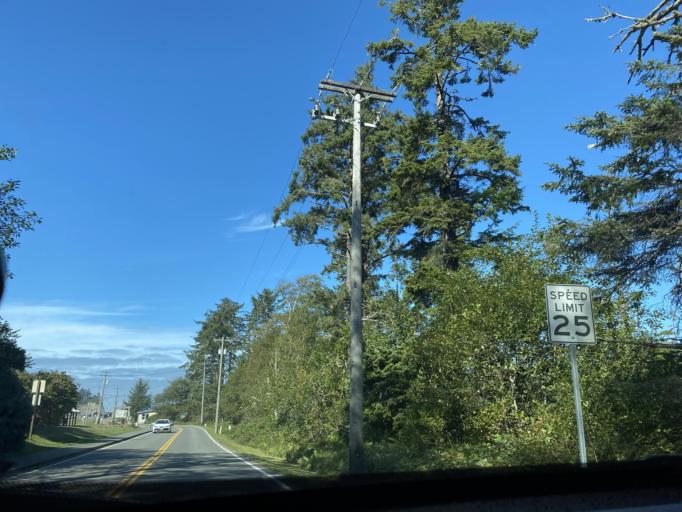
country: US
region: Washington
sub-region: Clallam County
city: Forks
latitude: 47.9056
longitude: -124.6310
